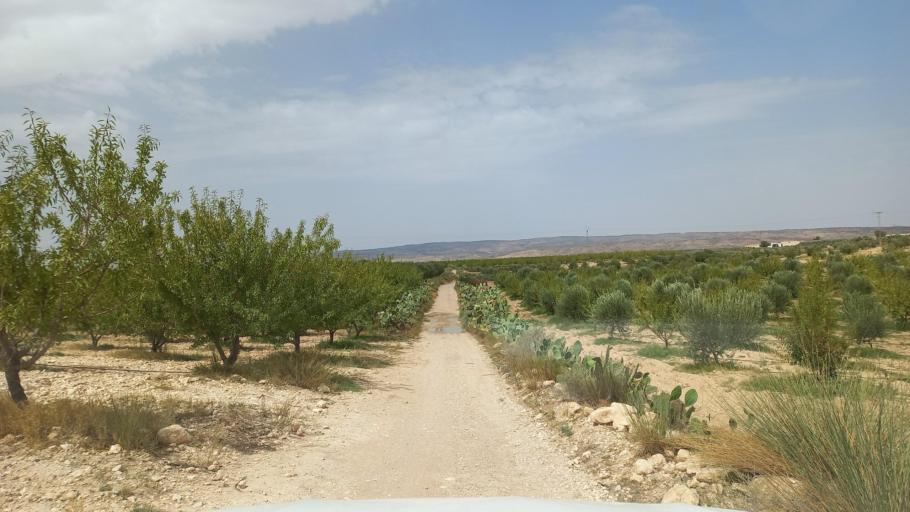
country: TN
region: Al Qasrayn
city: Kasserine
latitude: 35.2842
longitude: 9.0103
